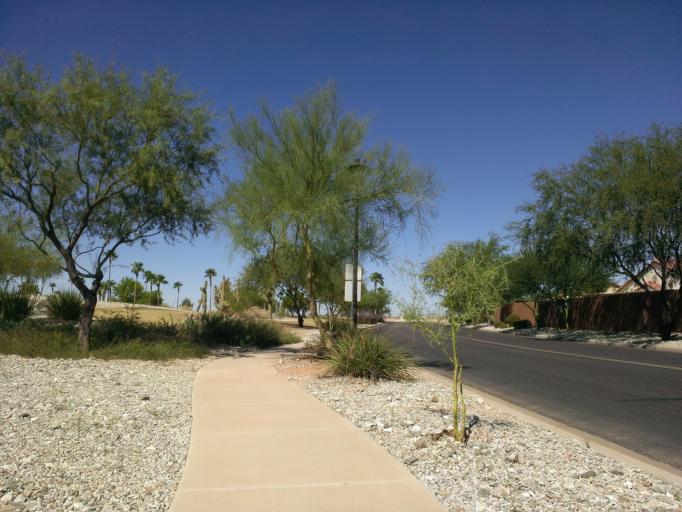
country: US
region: Arizona
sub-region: Pinal County
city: Arizona City
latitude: 32.8114
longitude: -111.6449
